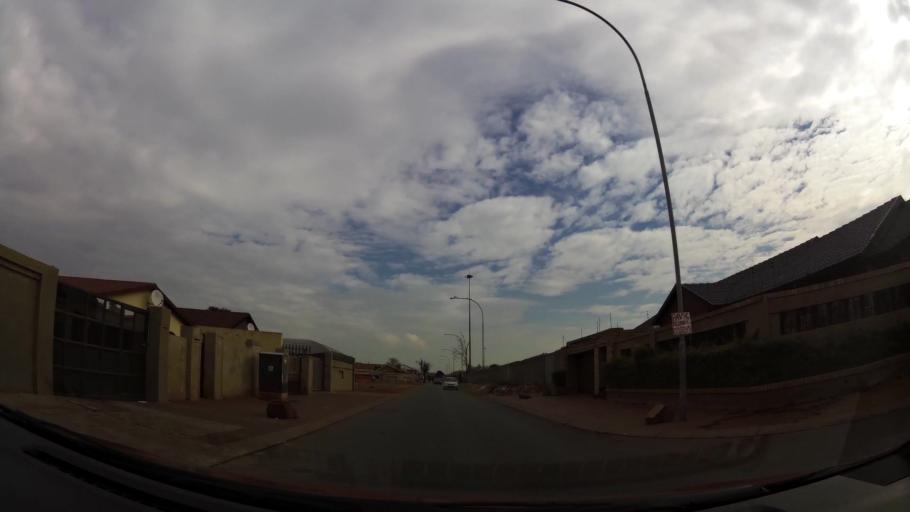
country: ZA
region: Gauteng
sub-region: City of Johannesburg Metropolitan Municipality
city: Soweto
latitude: -26.2707
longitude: 27.8295
